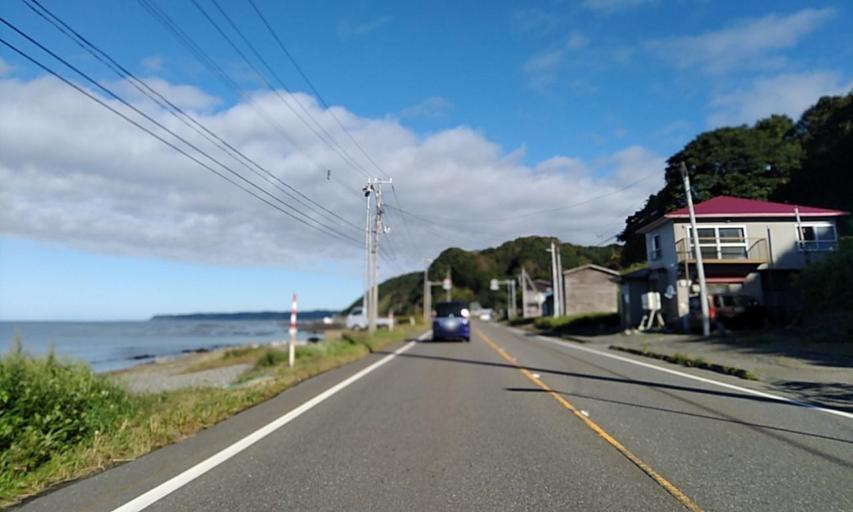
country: JP
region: Hokkaido
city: Shizunai-furukawacho
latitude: 42.2754
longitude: 142.4760
